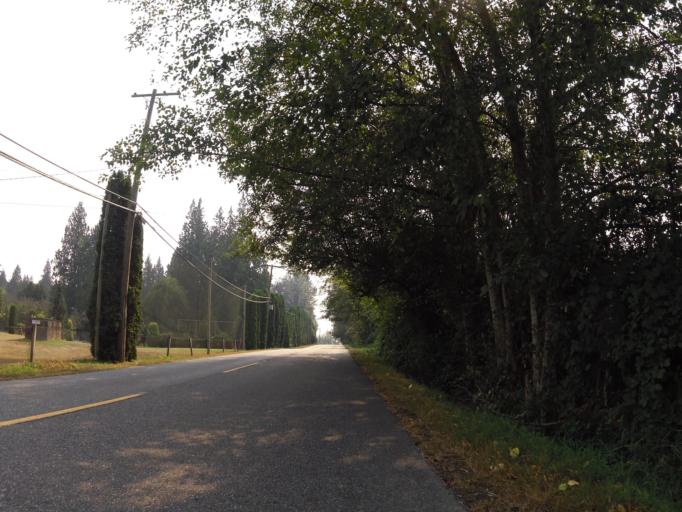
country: US
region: Washington
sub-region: Whatcom County
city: Blaine
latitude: 49.0210
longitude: -122.7572
